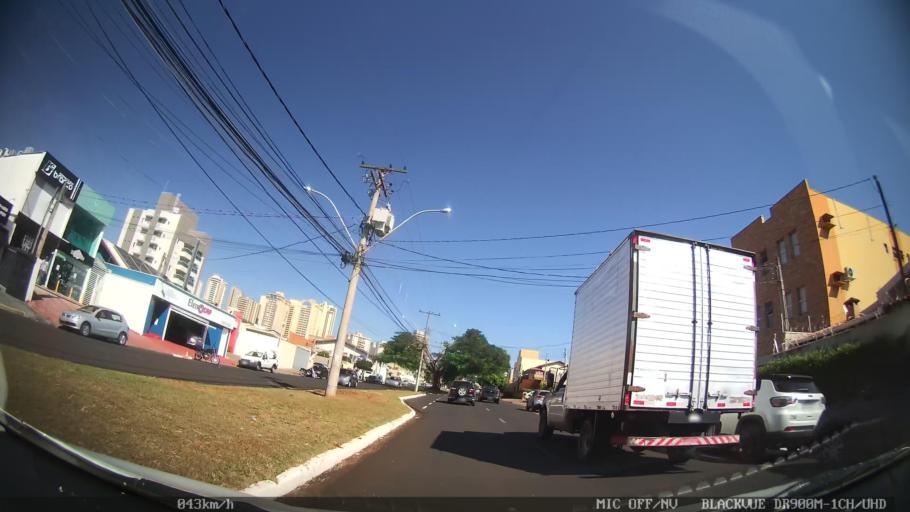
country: BR
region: Sao Paulo
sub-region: Ribeirao Preto
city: Ribeirao Preto
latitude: -21.2011
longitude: -47.8044
